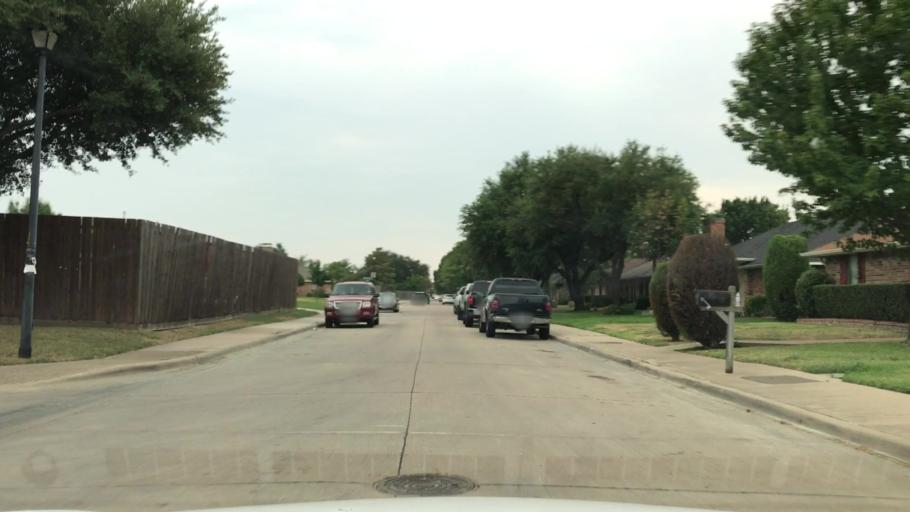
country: US
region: Texas
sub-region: Dallas County
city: Carrollton
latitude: 32.9917
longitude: -96.8736
